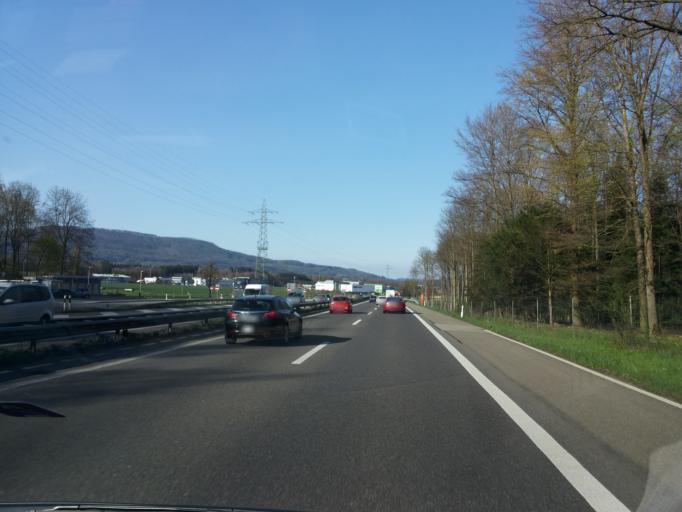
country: CH
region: Aargau
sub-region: Bezirk Aarau
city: Graenichen
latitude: 47.3798
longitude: 8.1093
